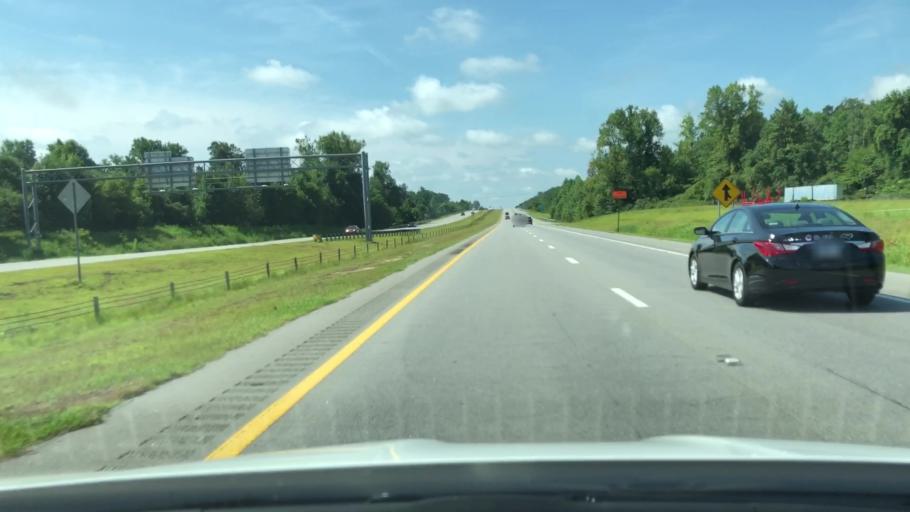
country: US
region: North Carolina
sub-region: Martin County
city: Williamston
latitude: 35.8394
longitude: -77.0533
